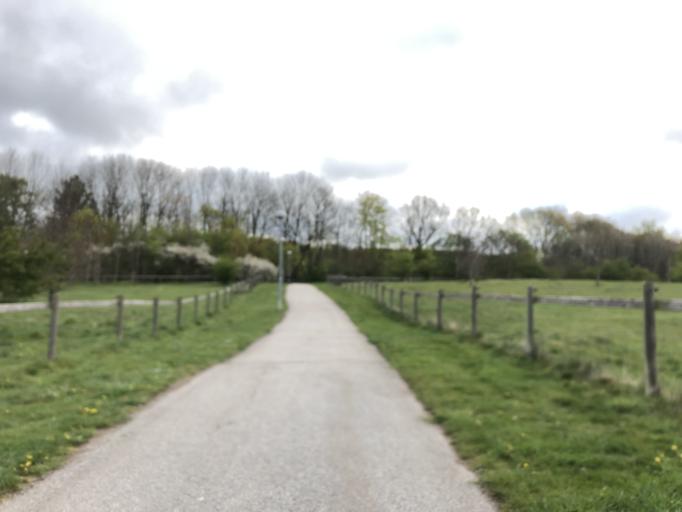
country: SE
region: Skane
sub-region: Lunds Kommun
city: Genarp
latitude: 55.6705
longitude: 13.3541
